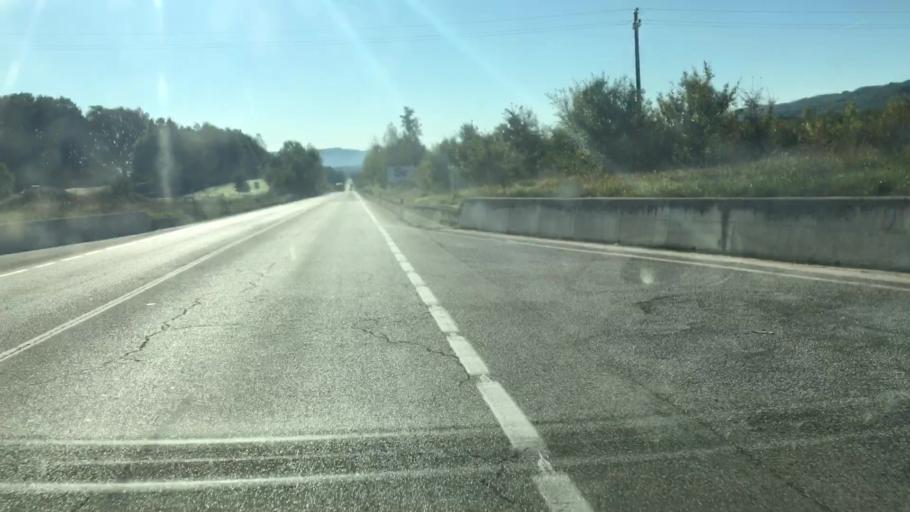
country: IT
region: Molise
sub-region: Provincia di Campobasso
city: Vinchiaturo
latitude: 41.4521
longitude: 14.5868
